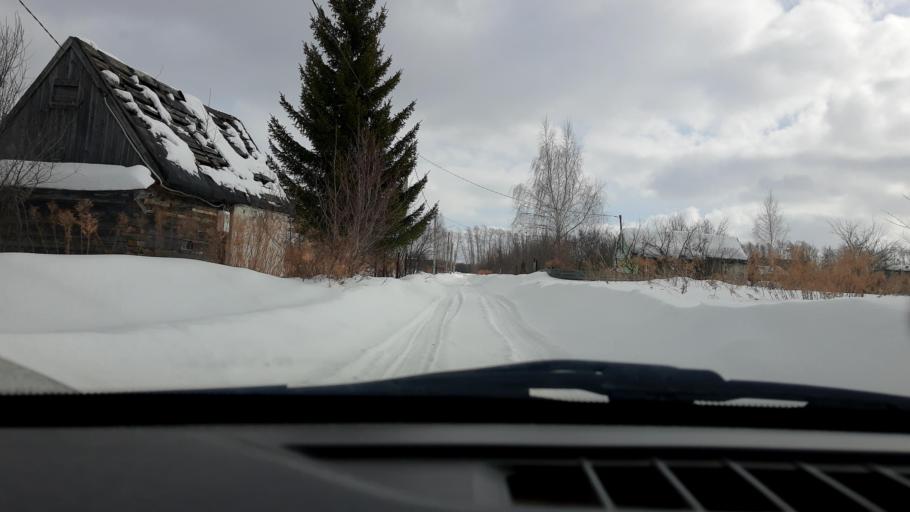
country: RU
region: Bashkortostan
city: Iglino
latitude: 54.7312
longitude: 56.2303
